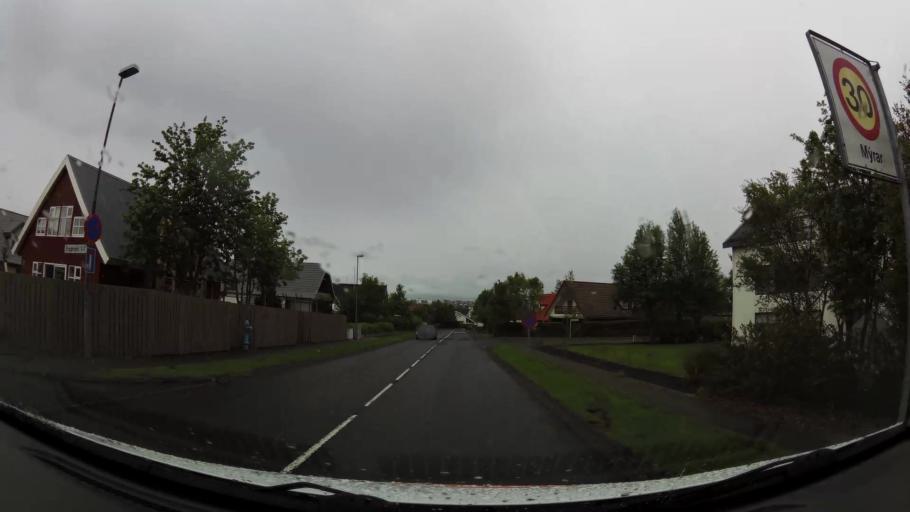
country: IS
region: Capital Region
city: Gardabaer
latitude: 64.0922
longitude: -21.9172
